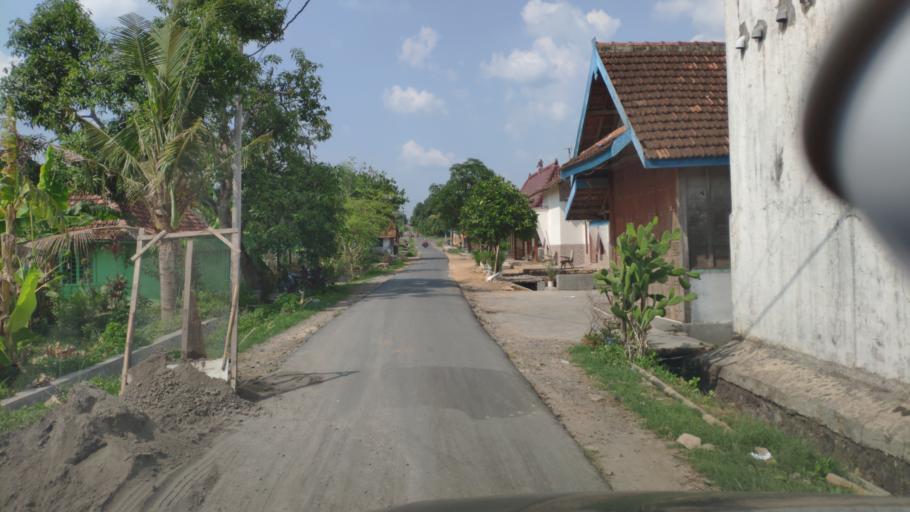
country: ID
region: Central Java
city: Jagong
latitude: -7.0491
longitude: 111.2508
